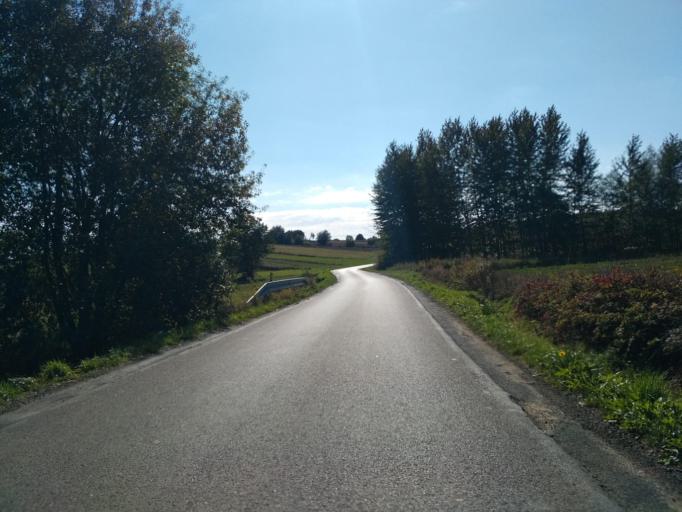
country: PL
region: Subcarpathian Voivodeship
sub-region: Powiat debicki
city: Slotowa
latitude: 49.9564
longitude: 21.2937
